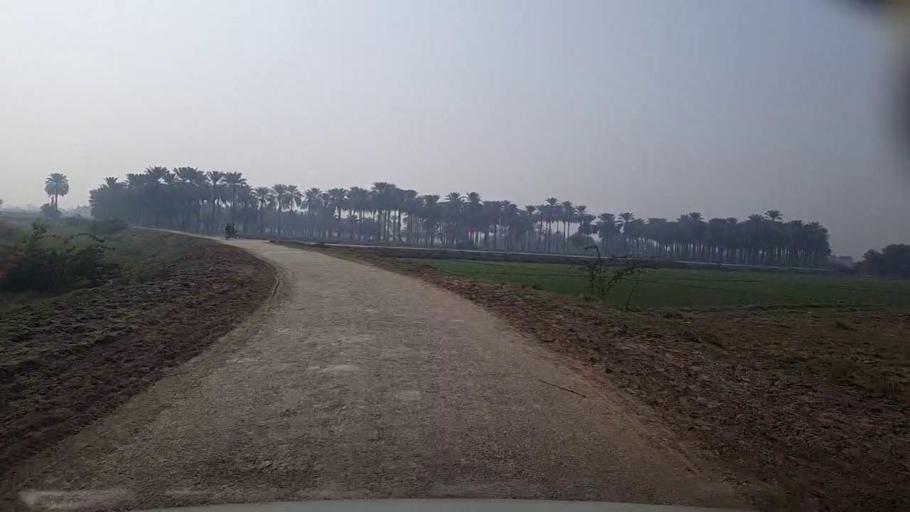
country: PK
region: Sindh
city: Setharja Old
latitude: 27.1925
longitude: 68.4768
